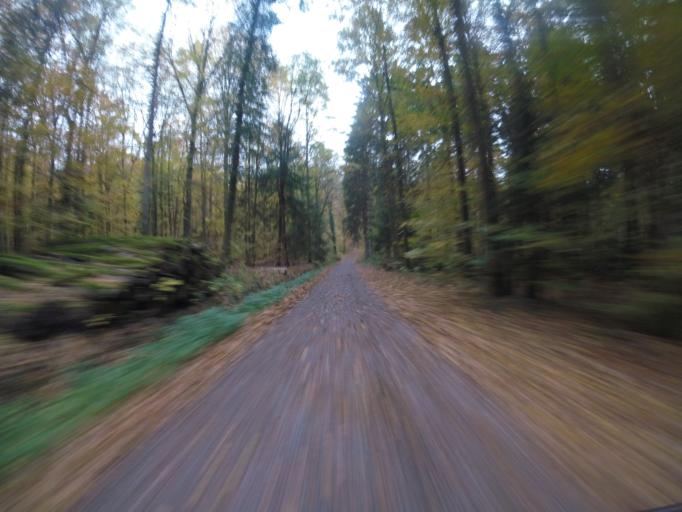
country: DE
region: Baden-Wuerttemberg
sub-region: Regierungsbezirk Stuttgart
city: Kirchberg an der Murr
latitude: 48.9747
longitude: 9.3565
